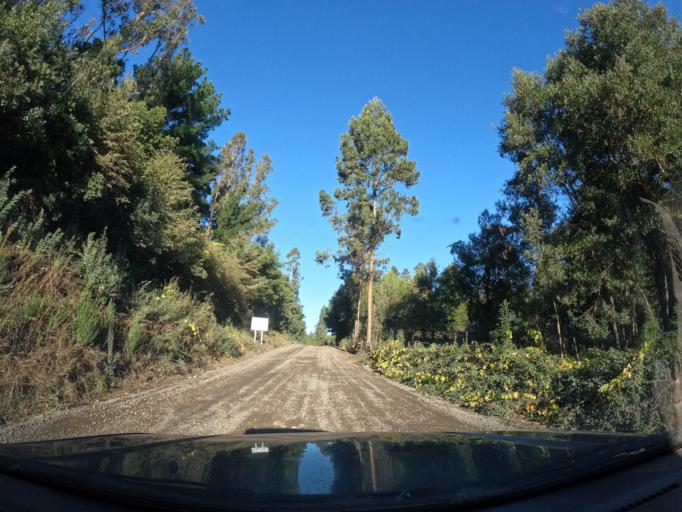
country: CL
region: Biobio
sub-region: Provincia de Concepcion
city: Chiguayante
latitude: -37.0212
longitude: -72.8898
